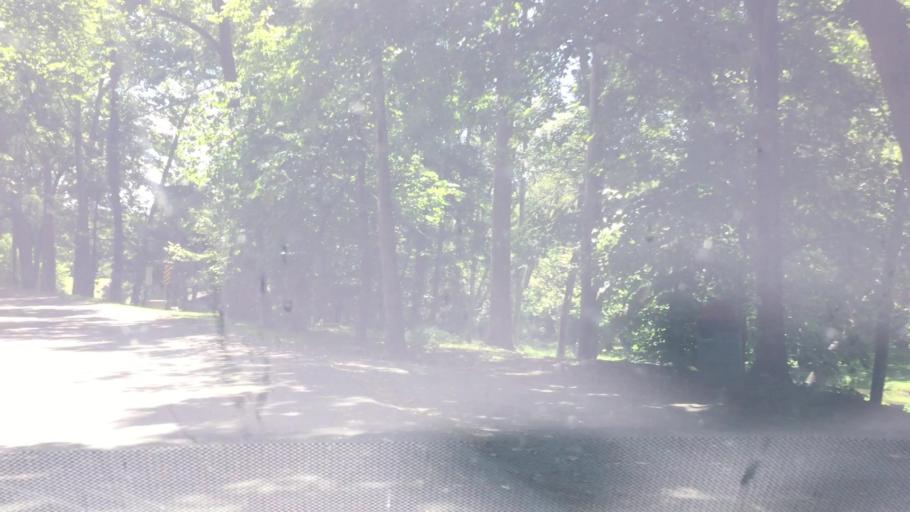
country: US
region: Virginia
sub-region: Pulaski County
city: Pulaski
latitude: 36.9516
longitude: -80.9014
